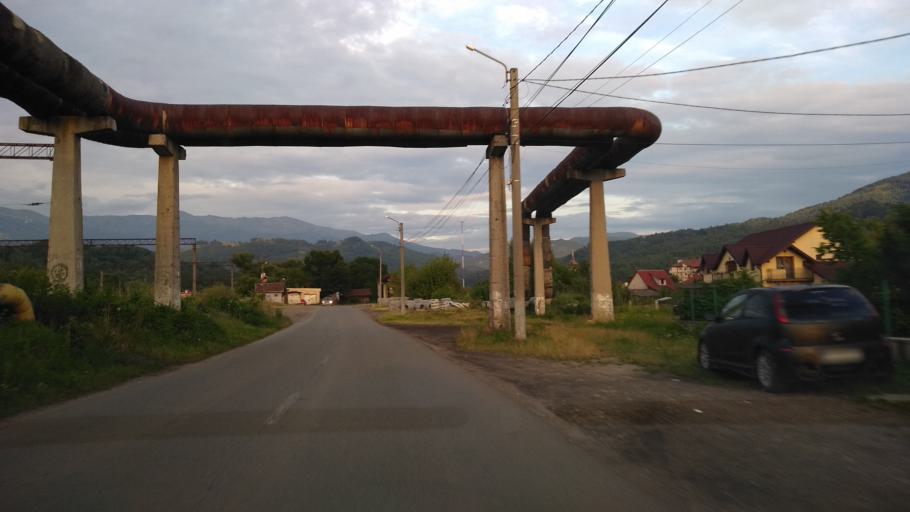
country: RO
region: Hunedoara
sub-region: Comuna Aninoasa
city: Iscroni
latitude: 45.3789
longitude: 23.3328
